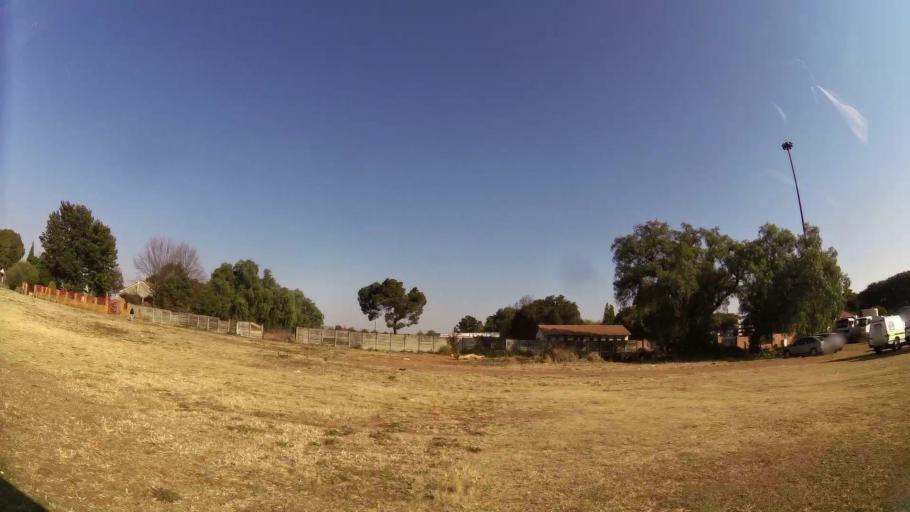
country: ZA
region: Gauteng
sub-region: Ekurhuleni Metropolitan Municipality
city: Boksburg
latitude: -26.2304
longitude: 28.2255
